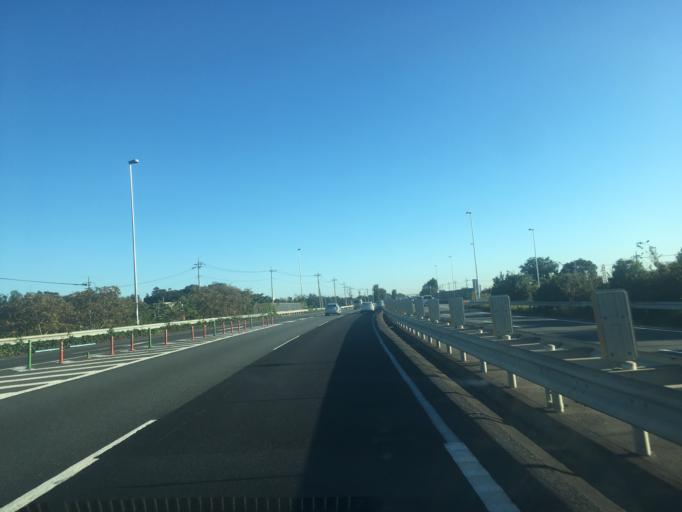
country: JP
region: Saitama
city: Sayama
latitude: 35.8525
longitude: 139.3667
